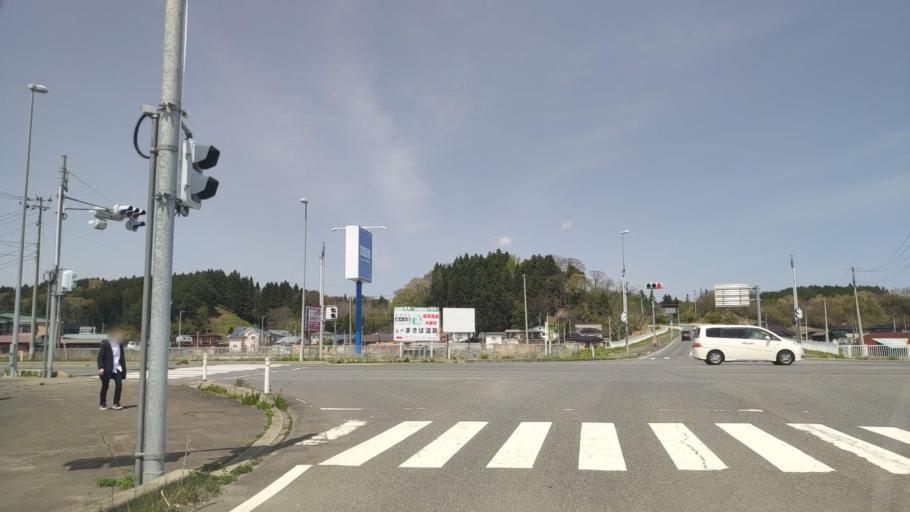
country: JP
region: Aomori
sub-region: Hachinohe Shi
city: Uchimaru
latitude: 40.5171
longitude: 141.4268
